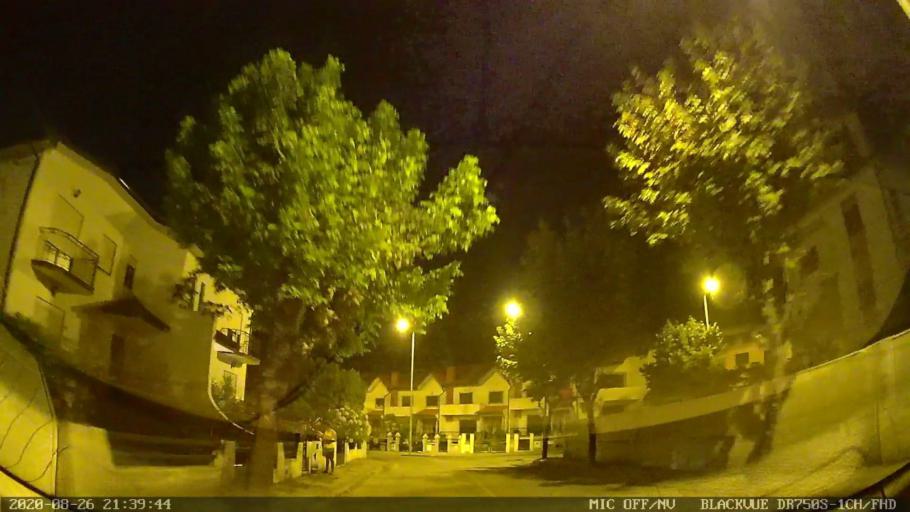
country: PT
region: Viseu
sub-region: Viseu
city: Rio de Loba
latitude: 40.6628
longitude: -7.8866
